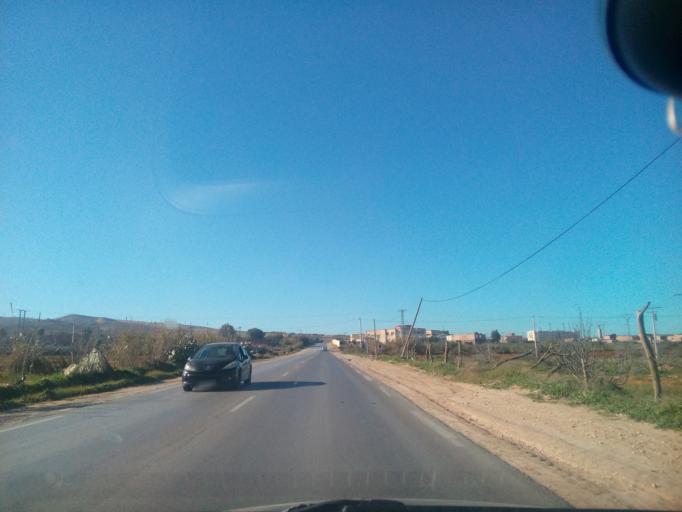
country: DZ
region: Relizane
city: Relizane
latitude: 35.9035
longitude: 0.5197
